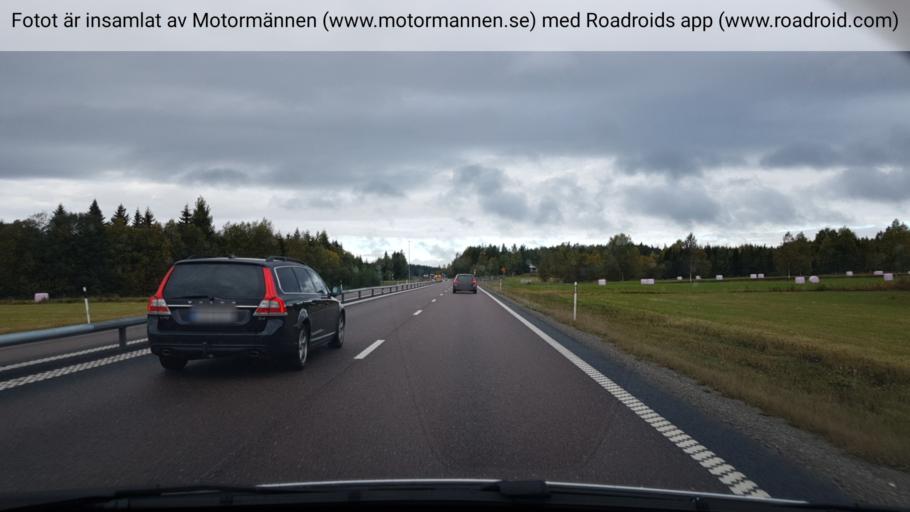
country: SE
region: Vaesternorrland
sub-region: OErnskoeldsviks Kommun
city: Ornskoldsvik
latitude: 63.3007
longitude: 18.8634
